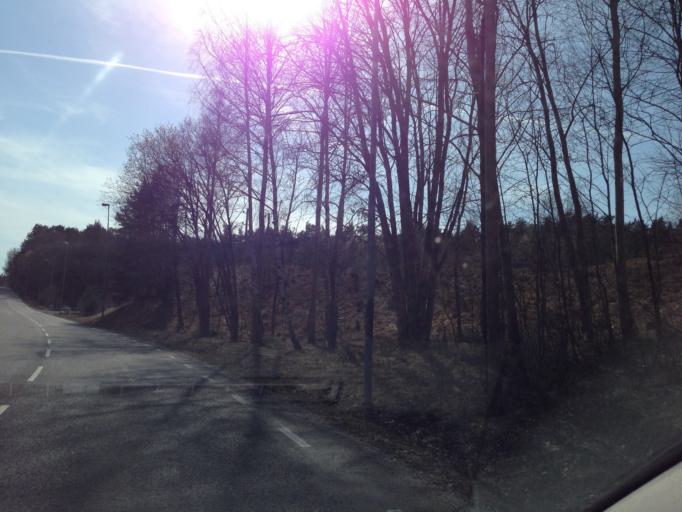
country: SE
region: Stockholm
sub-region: Botkyrka Kommun
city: Eriksberg
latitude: 59.2410
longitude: 17.7834
